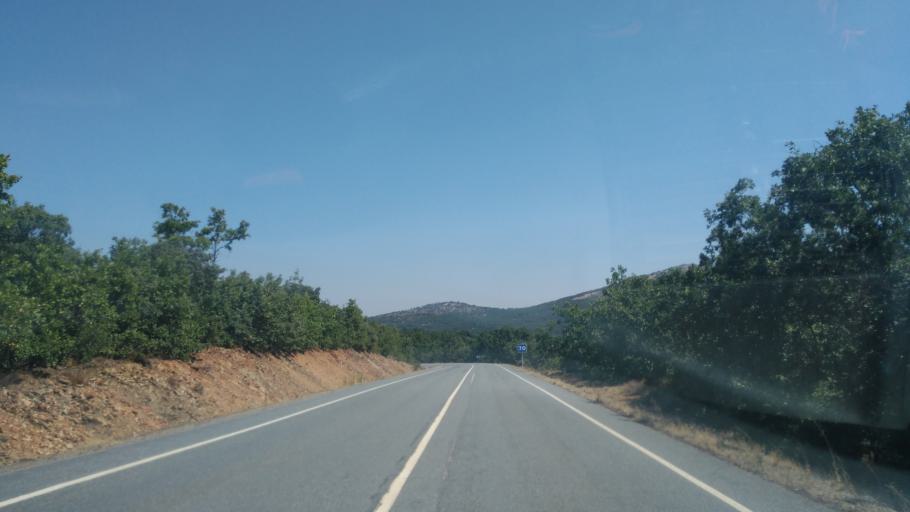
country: ES
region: Castille and Leon
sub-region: Provincia de Salamanca
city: Aldeanueva de la Sierra
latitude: 40.6012
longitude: -6.0933
